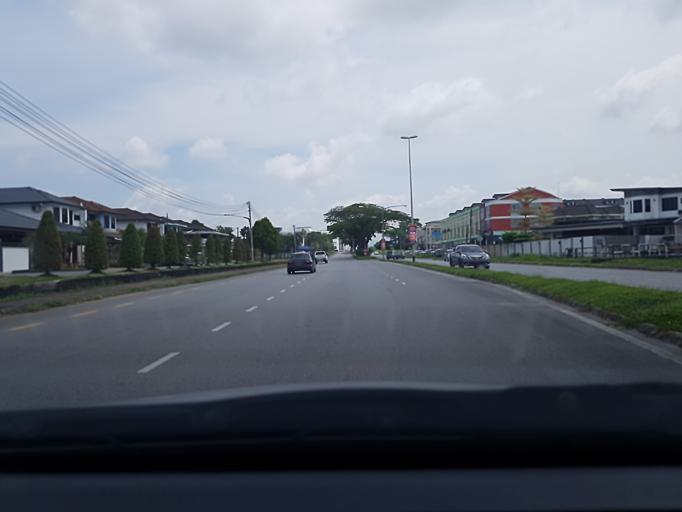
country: MY
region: Sarawak
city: Kuching
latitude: 1.5183
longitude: 110.3615
